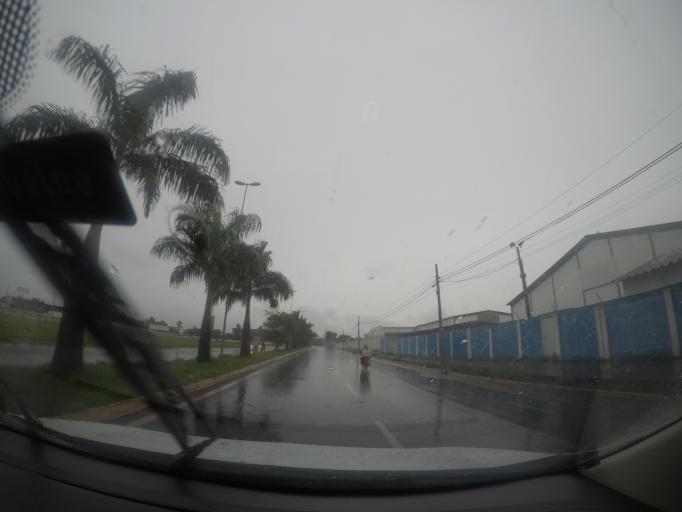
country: BR
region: Goias
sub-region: Goiania
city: Goiania
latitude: -16.6464
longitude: -49.3123
